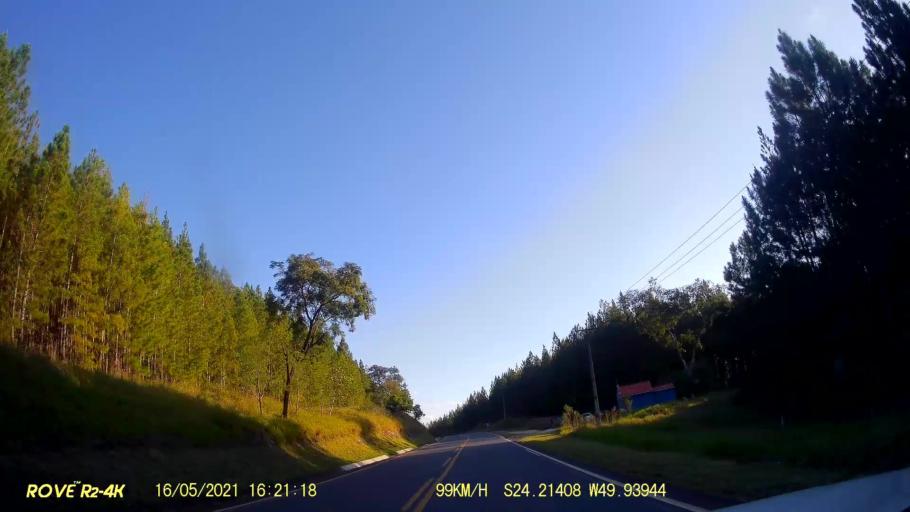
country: BR
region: Parana
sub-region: Jaguariaiva
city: Jaguariaiva
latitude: -24.2143
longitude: -49.9396
